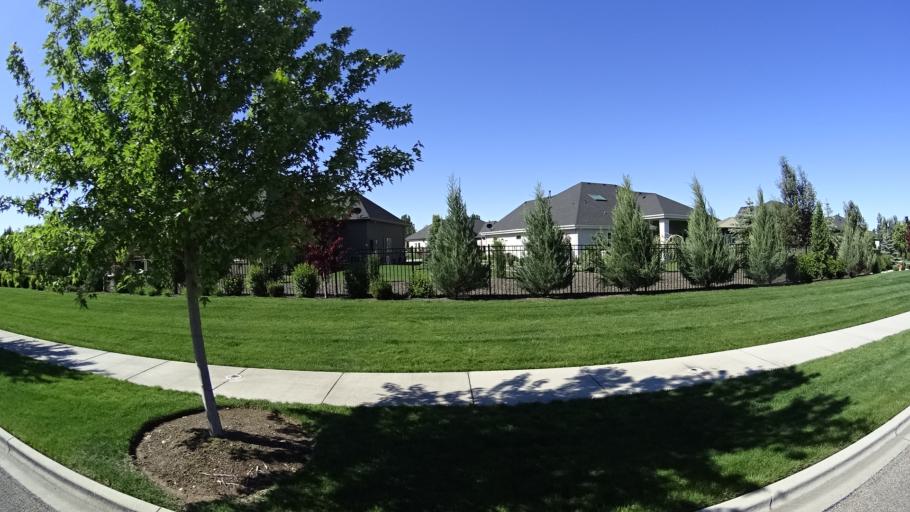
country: US
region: Idaho
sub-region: Ada County
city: Eagle
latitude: 43.6675
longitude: -116.3980
